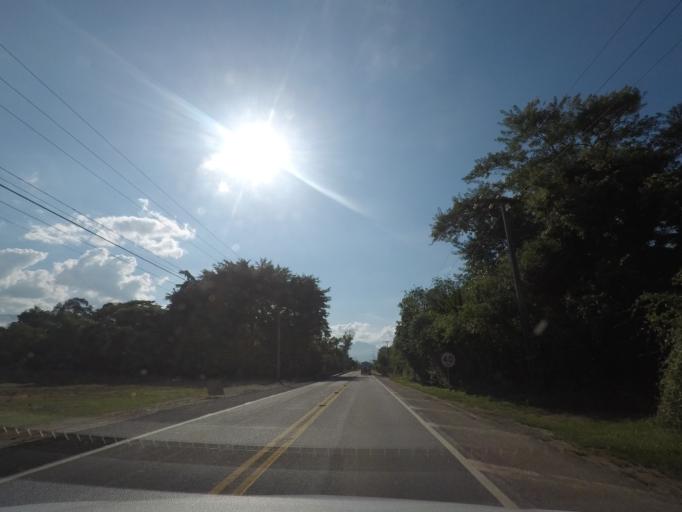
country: BR
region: Parana
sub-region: Antonina
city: Antonina
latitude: -25.5005
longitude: -48.8173
